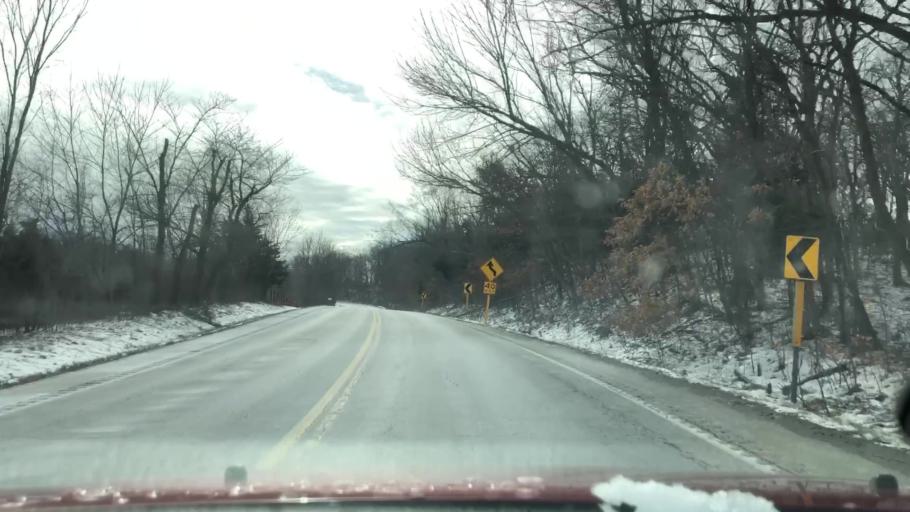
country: US
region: Missouri
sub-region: Jackson County
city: Lone Jack
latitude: 38.8960
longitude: -94.1353
